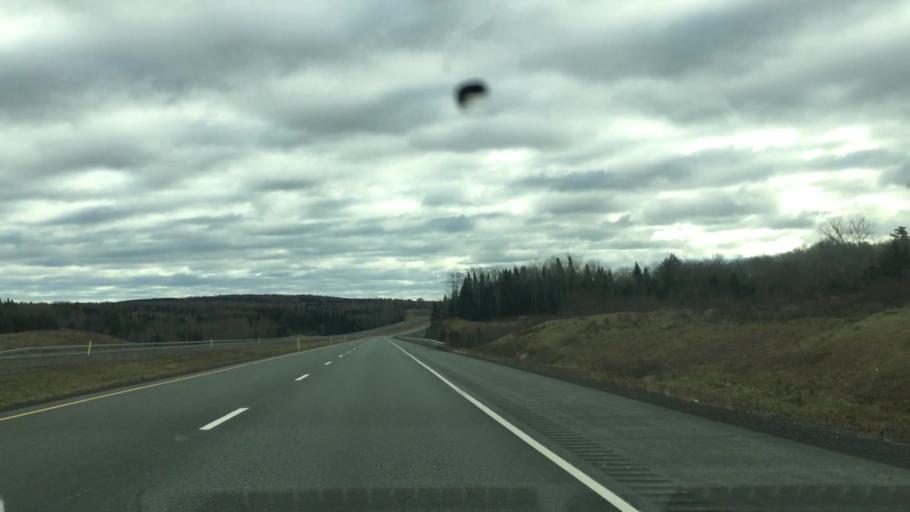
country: CA
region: New Brunswick
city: Florenceville-Bristol
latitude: 46.5443
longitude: -67.7201
